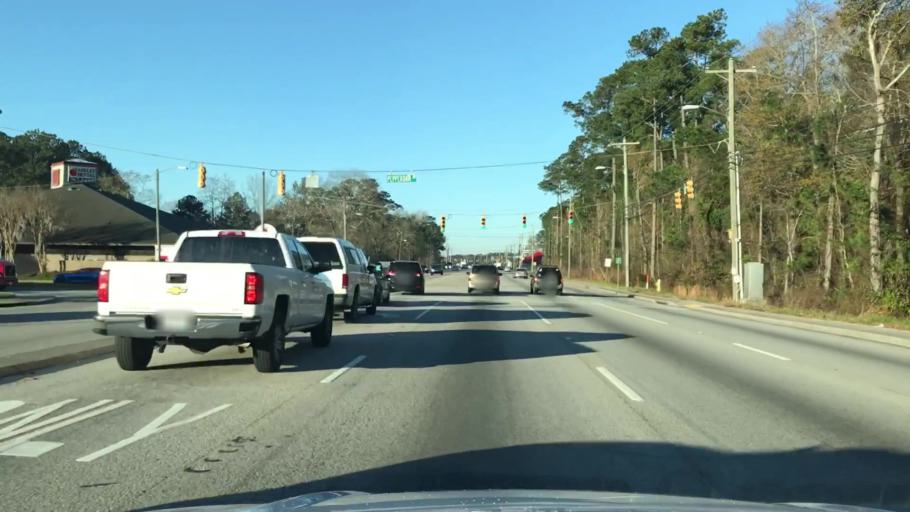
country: US
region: South Carolina
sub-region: Berkeley County
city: Hanahan
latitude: 32.9311
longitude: -80.0658
